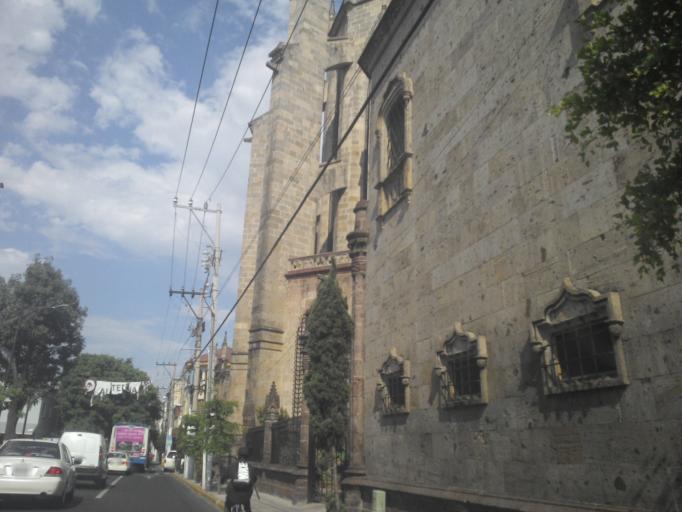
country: MX
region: Jalisco
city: Guadalajara
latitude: 20.6740
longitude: -103.3591
